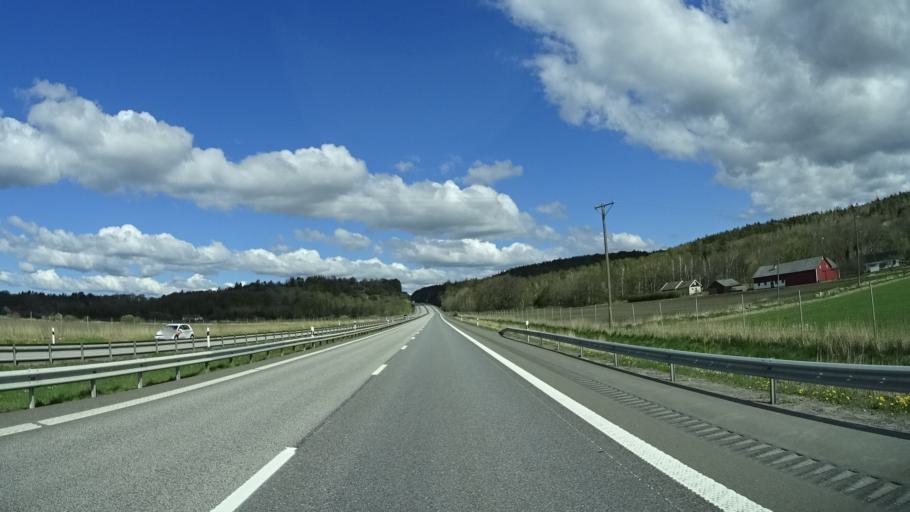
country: SE
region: Halland
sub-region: Kungsbacka Kommun
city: Frillesas
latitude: 57.3002
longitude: 12.2154
